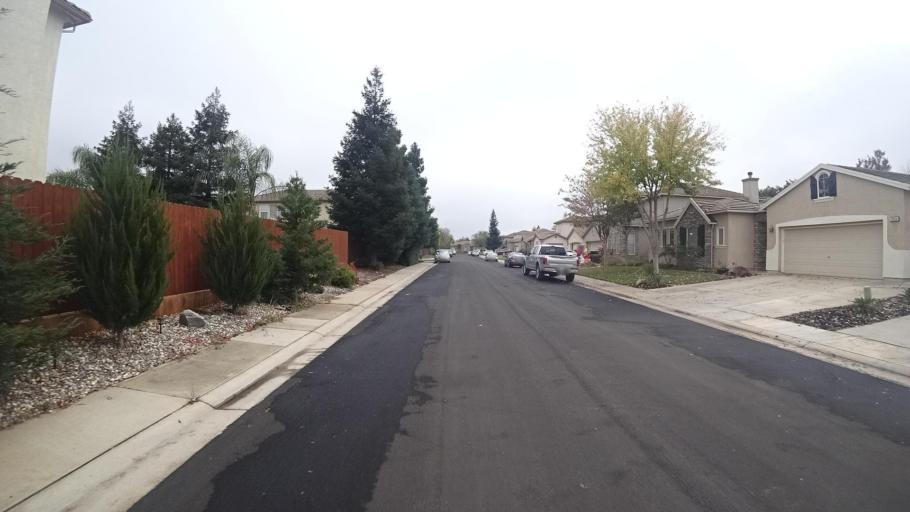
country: US
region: California
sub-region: Sacramento County
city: Elk Grove
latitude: 38.3936
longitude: -121.3470
